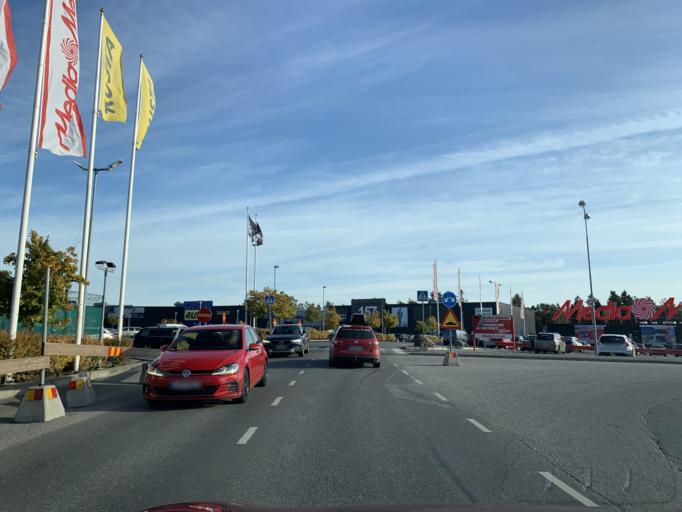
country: SE
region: Stockholm
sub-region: Haninge Kommun
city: Handen
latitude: 59.1983
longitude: 18.1258
